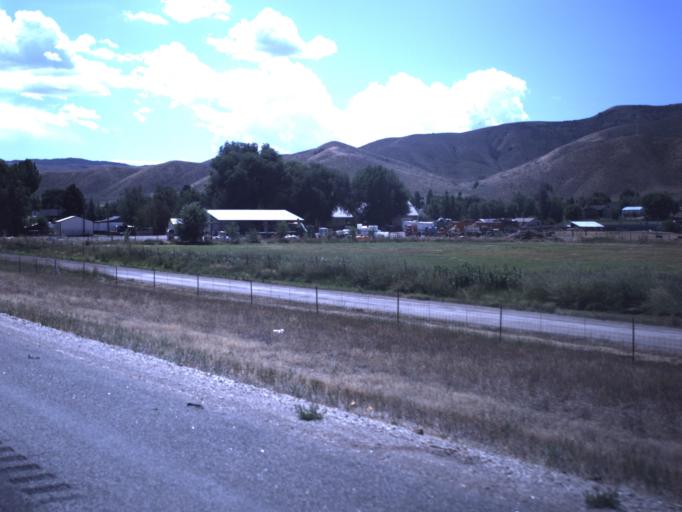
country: US
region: Utah
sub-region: Summit County
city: Coalville
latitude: 41.0209
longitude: -111.4938
